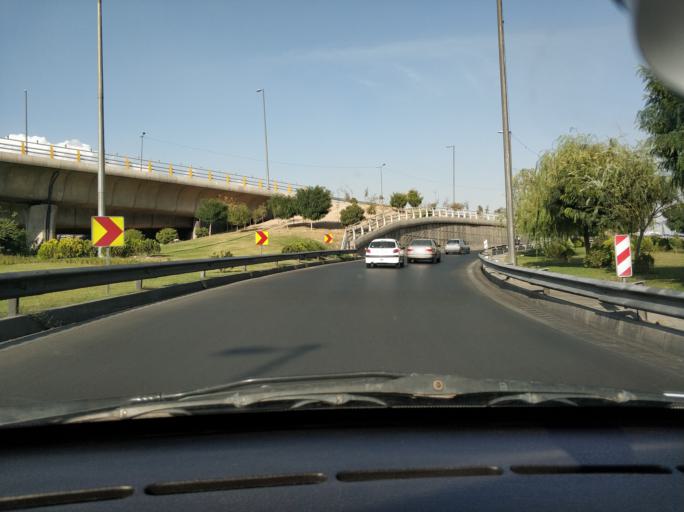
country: IR
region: Tehran
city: Tehran
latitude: 35.7113
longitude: 51.3371
